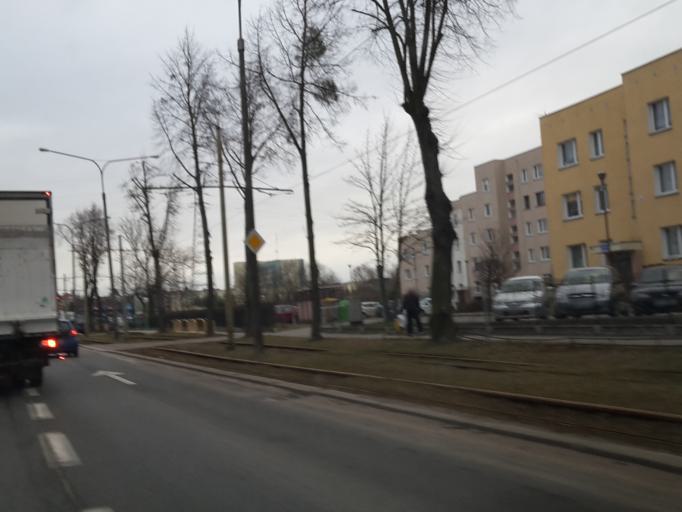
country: PL
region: Warmian-Masurian Voivodeship
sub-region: Powiat elblaski
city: Elblag
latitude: 54.1772
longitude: 19.4223
